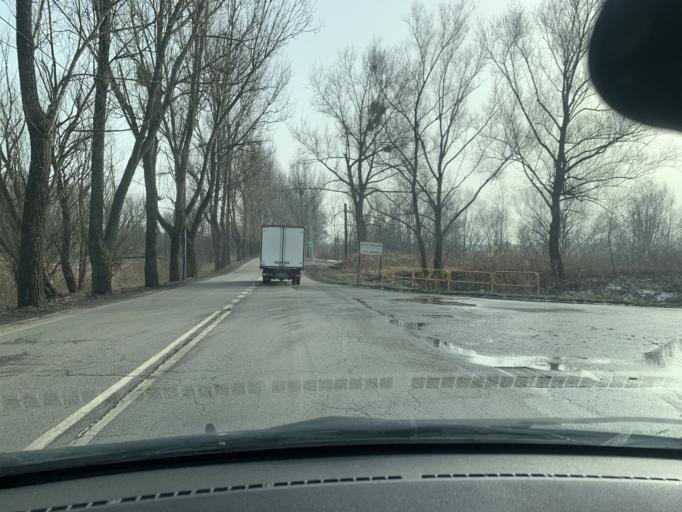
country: PL
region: Silesian Voivodeship
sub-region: Piekary Slaskie
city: Piekary Slaskie
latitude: 50.3659
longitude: 18.9165
